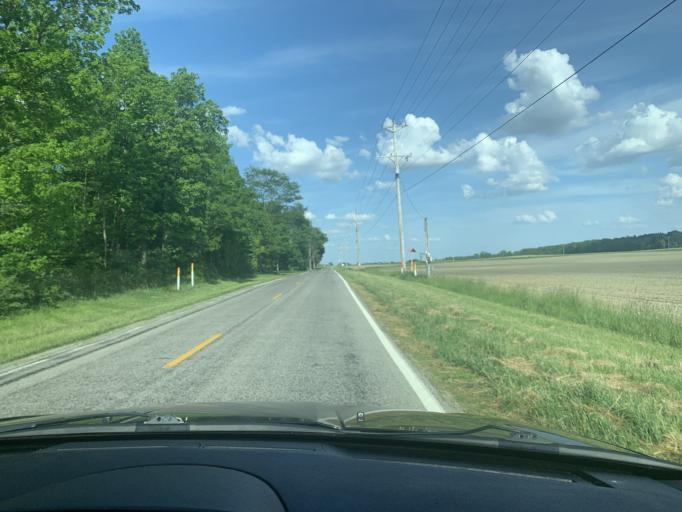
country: US
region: Ohio
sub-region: Logan County
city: De Graff
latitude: 40.2411
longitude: -83.9619
